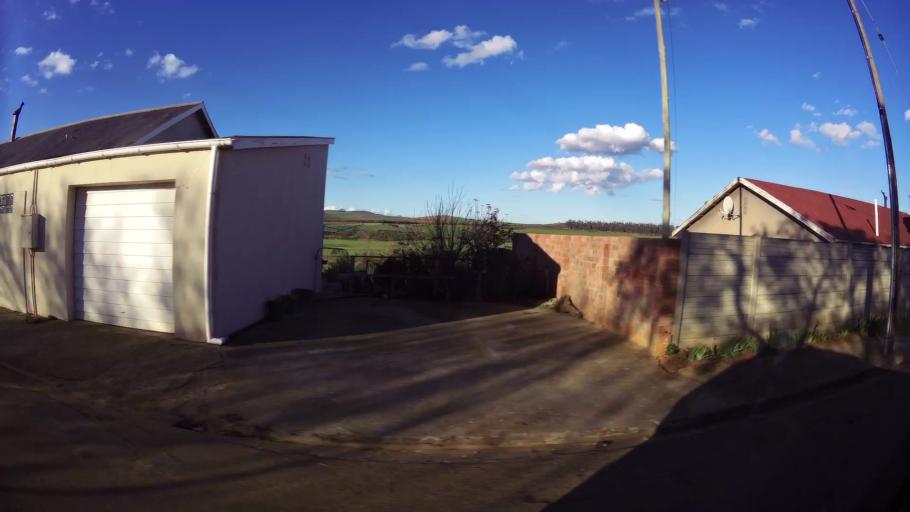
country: ZA
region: Western Cape
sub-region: Eden District Municipality
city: Riversdale
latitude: -34.0857
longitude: 20.9601
